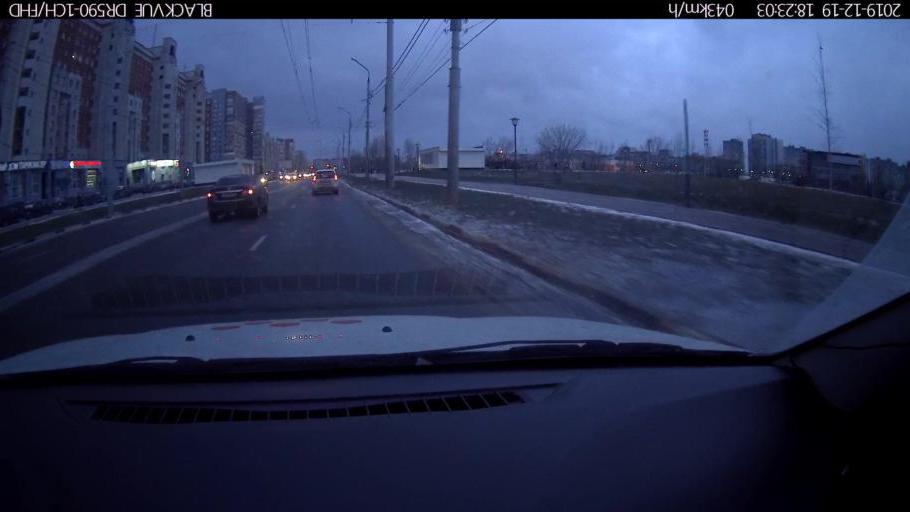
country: RU
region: Nizjnij Novgorod
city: Nizhniy Novgorod
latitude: 56.3339
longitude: 43.9463
